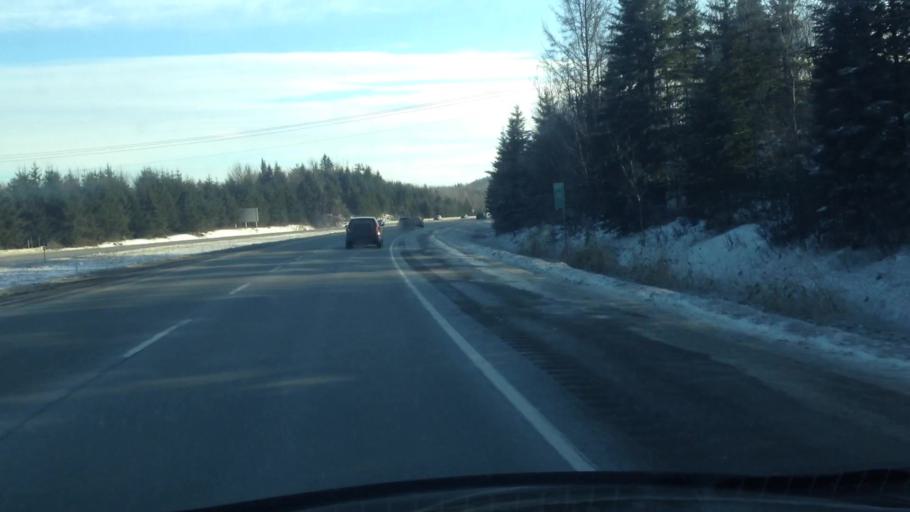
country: CA
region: Quebec
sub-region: Laurentides
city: Prevost
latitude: 45.8739
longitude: -74.0881
